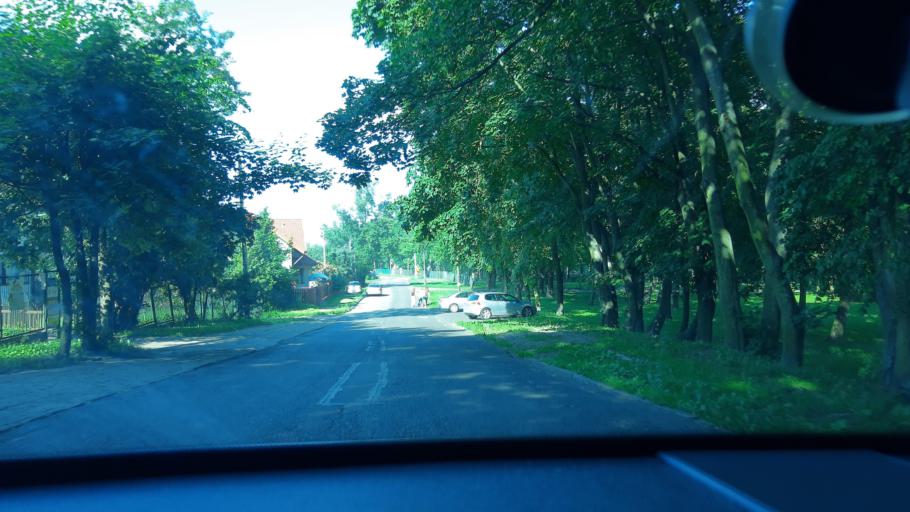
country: PL
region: Lodz Voivodeship
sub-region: Powiat sieradzki
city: Sieradz
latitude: 51.6010
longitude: 18.7360
